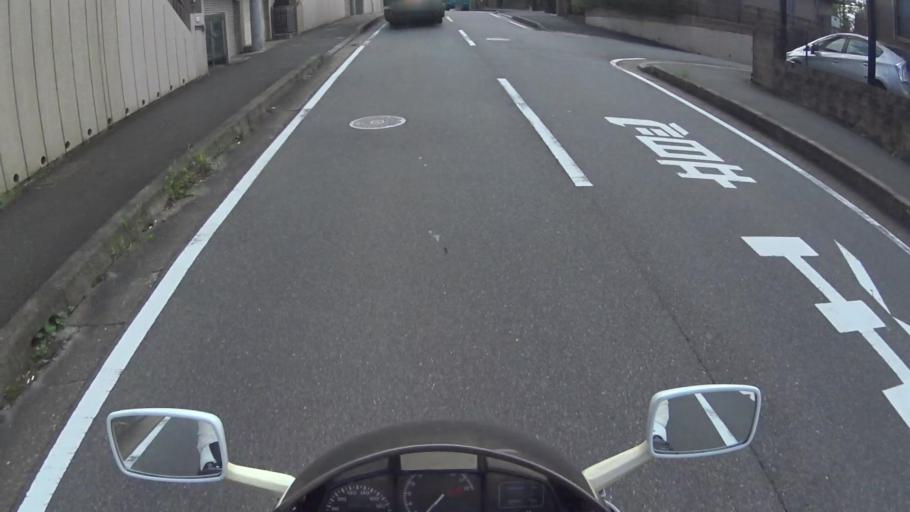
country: JP
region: Kyoto
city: Uji
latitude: 34.9267
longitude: 135.8141
